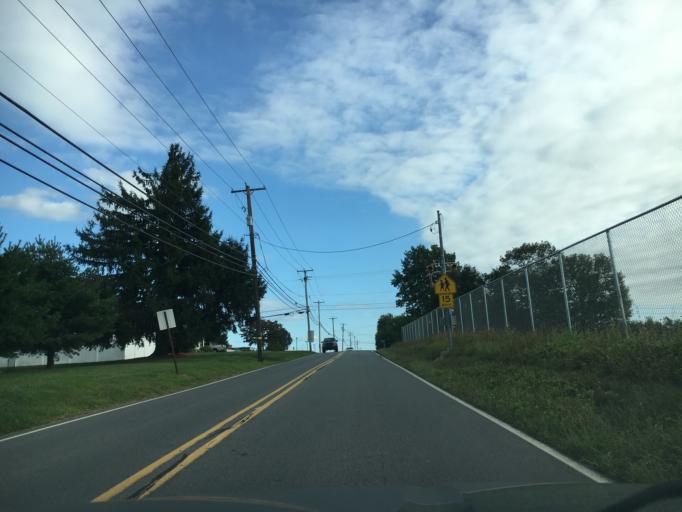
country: US
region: Pennsylvania
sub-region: Berks County
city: Topton
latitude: 40.5922
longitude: -75.7114
